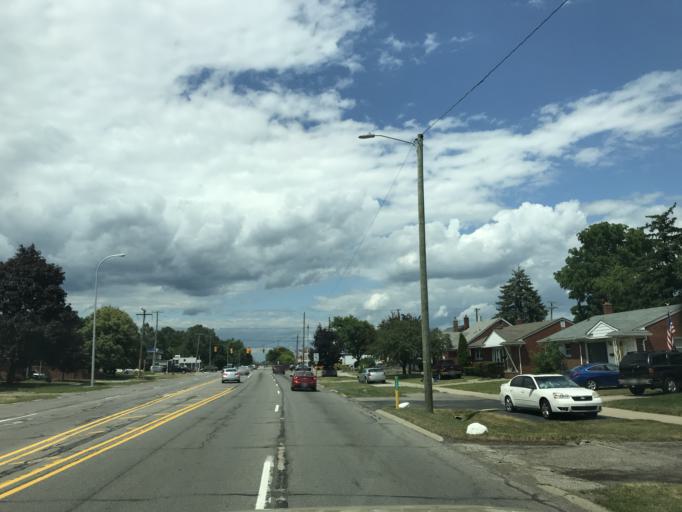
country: US
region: Michigan
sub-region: Wayne County
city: Redford
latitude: 42.3686
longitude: -83.3133
